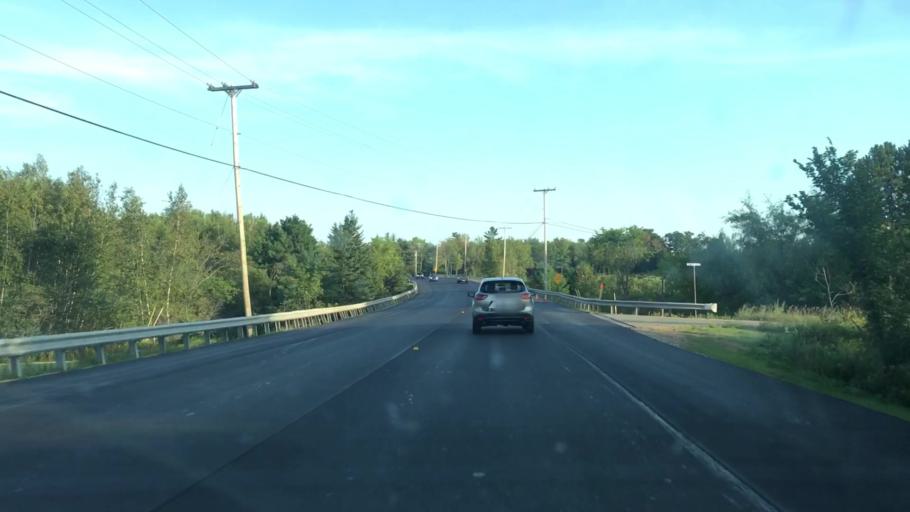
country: US
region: Maine
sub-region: Penobscot County
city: Hampden
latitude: 44.7692
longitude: -68.8564
